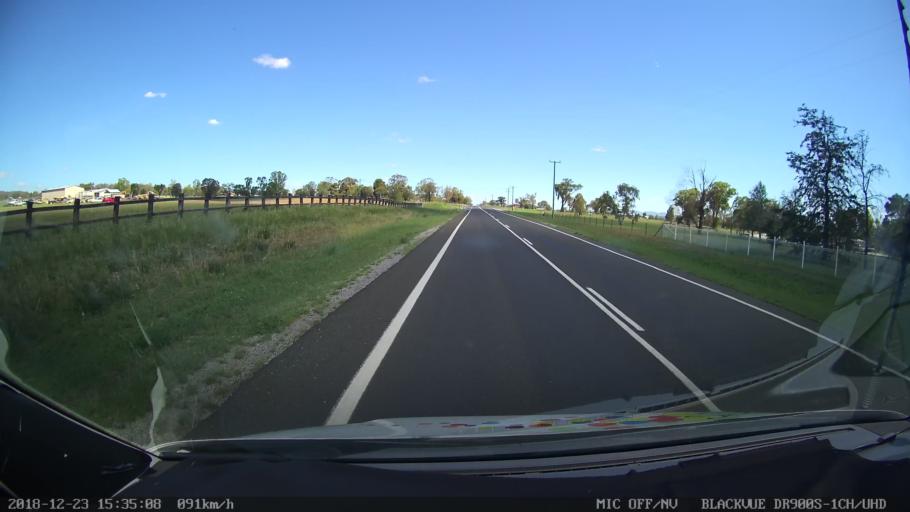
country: AU
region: New South Wales
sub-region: Tamworth Municipality
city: Tamworth
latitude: -31.0232
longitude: 150.8812
